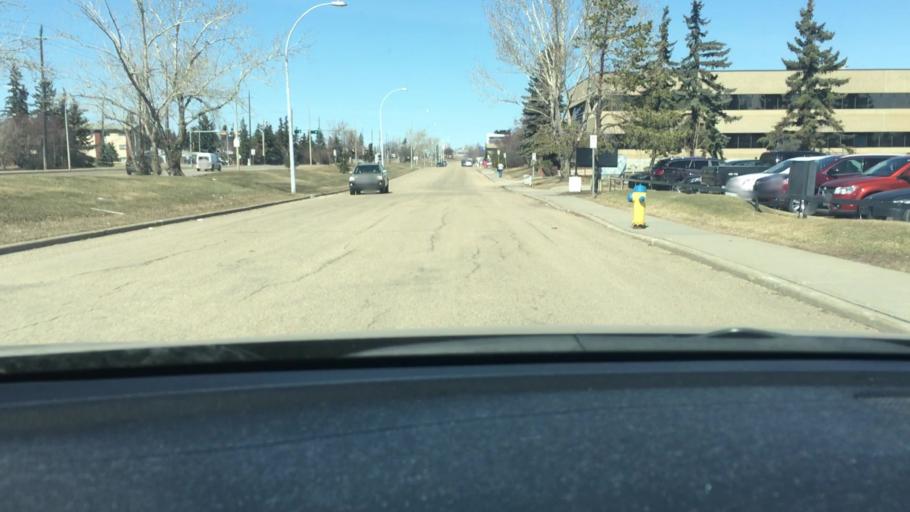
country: CA
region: Alberta
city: Edmonton
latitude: 53.5324
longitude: -113.4181
